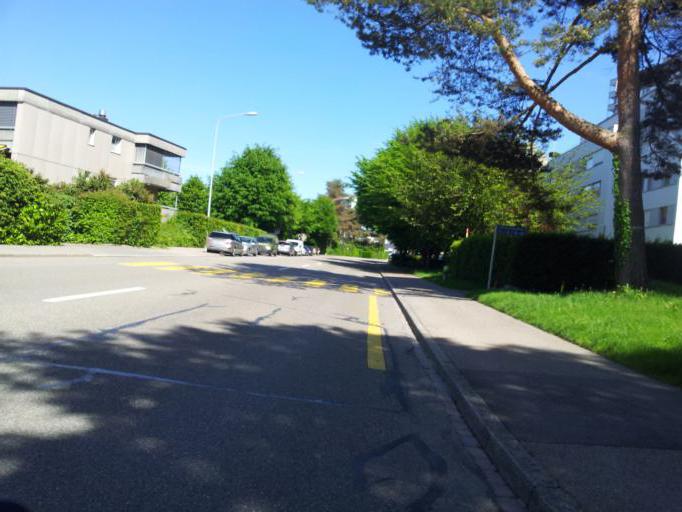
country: CH
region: Zurich
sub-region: Bezirk Dietikon
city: Dietikon / Schoenenwerd
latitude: 47.3944
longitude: 8.4261
